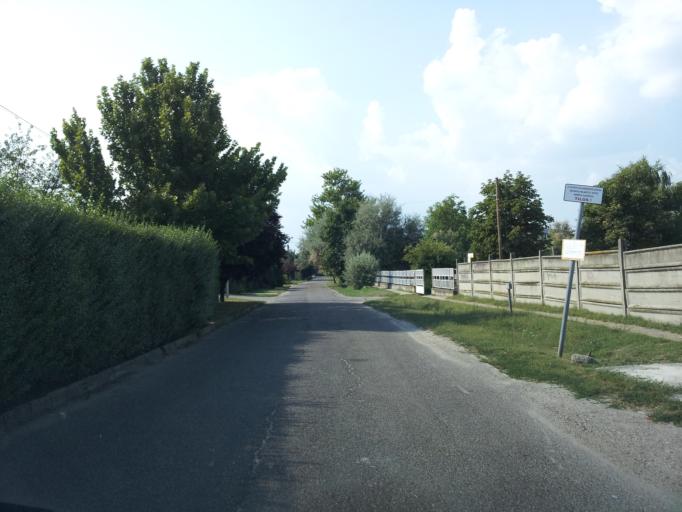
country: HU
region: Pest
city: Szigethalom
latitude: 47.3240
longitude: 18.9943
